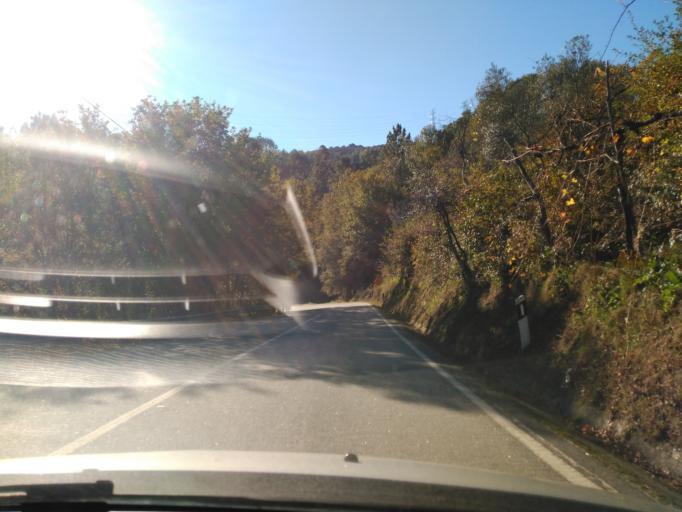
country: PT
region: Braga
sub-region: Vieira do Minho
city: Vieira do Minho
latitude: 41.6790
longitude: -8.1070
